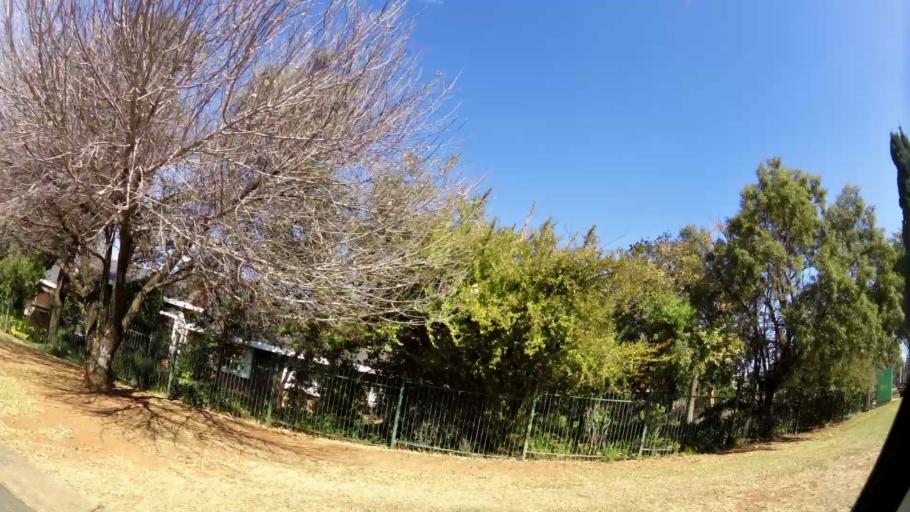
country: ZA
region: Gauteng
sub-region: City of Tshwane Metropolitan Municipality
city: Pretoria
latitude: -25.7728
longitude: 28.2707
